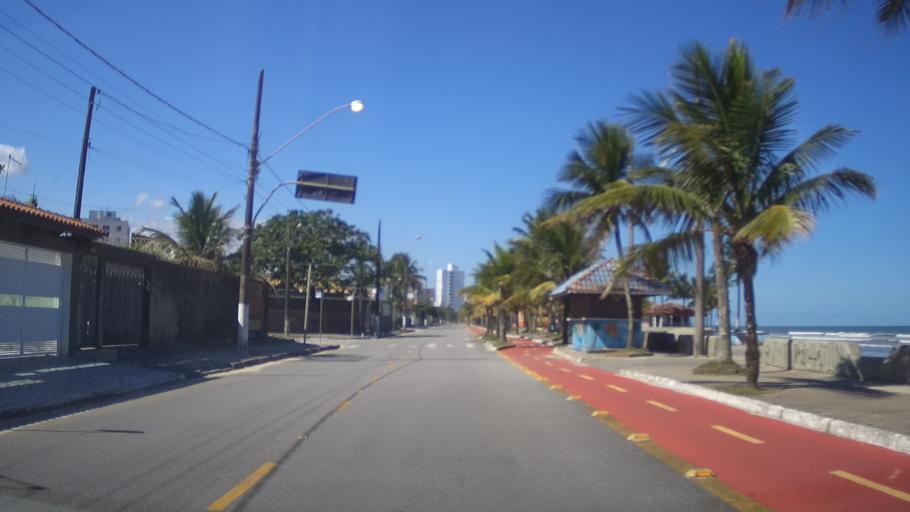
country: BR
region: Sao Paulo
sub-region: Mongagua
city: Mongagua
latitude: -24.1226
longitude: -46.6724
